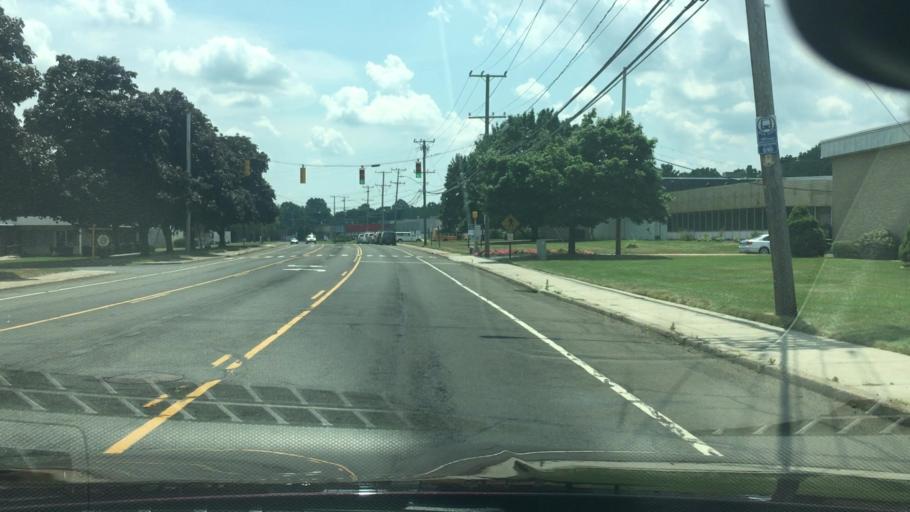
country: US
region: Connecticut
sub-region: Hartford County
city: New Britain
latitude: 41.6648
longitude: -72.7553
